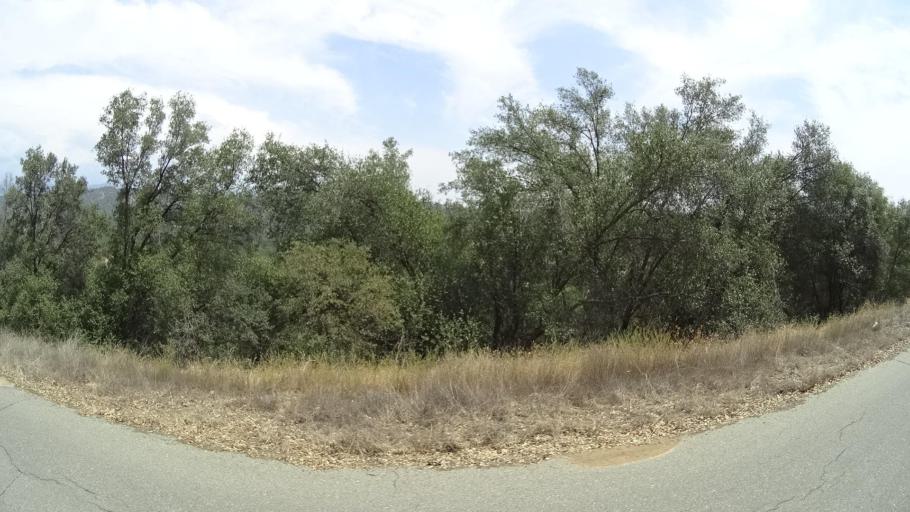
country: US
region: California
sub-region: Mariposa County
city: Mariposa
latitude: 37.4154
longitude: -119.8721
